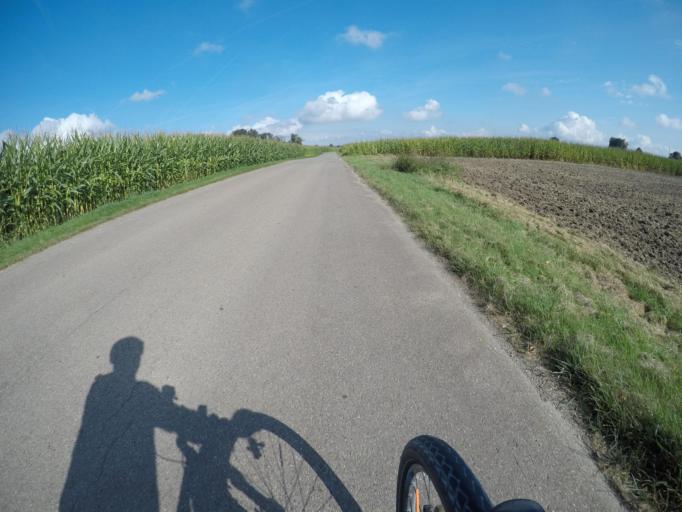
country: DE
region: Bavaria
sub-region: Swabia
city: Buttenwiesen
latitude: 48.6469
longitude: 10.7332
